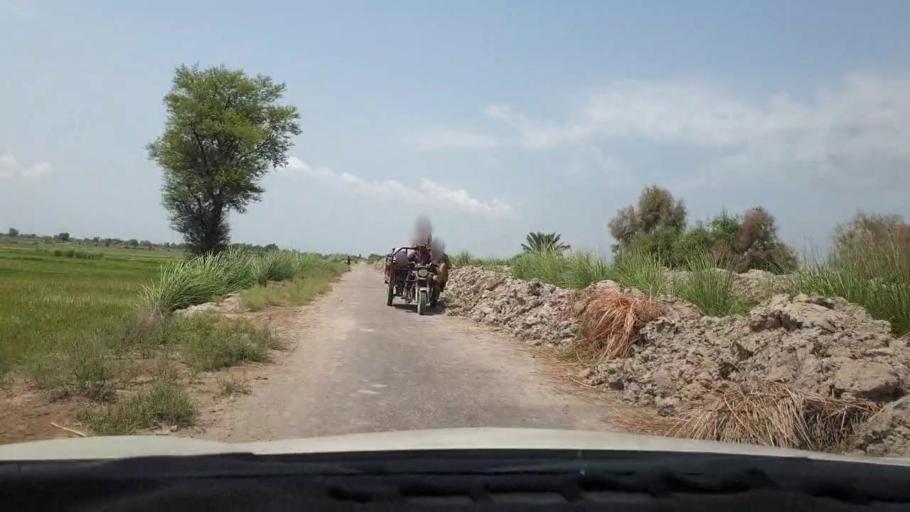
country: PK
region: Sindh
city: Ratodero
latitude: 27.8386
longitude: 68.2231
